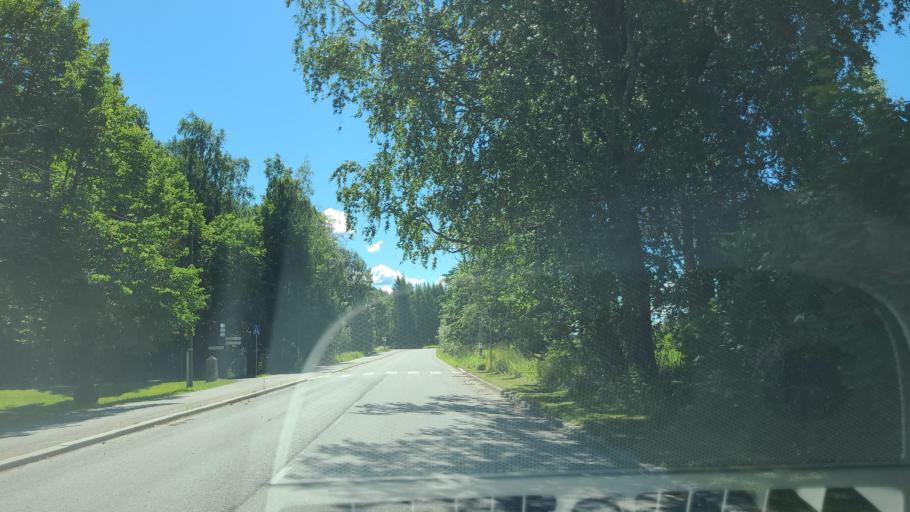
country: FI
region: Ostrobothnia
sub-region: Vaasa
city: Ristinummi
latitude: 63.0703
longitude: 21.7236
